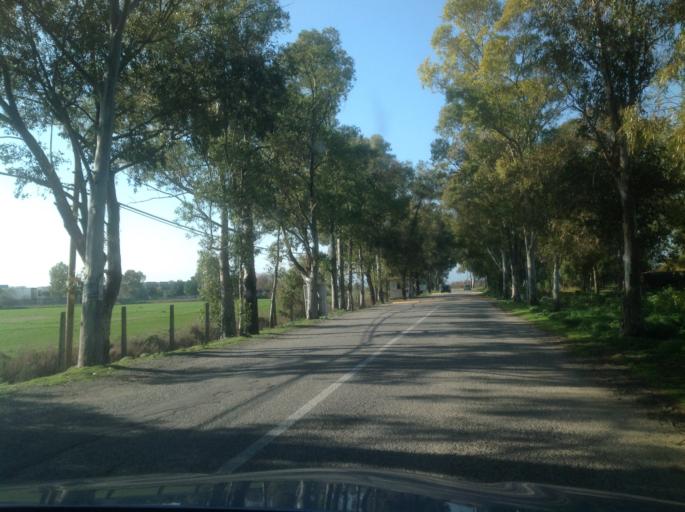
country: IT
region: Calabria
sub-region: Provincia di Cosenza
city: Sibari
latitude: 39.7261
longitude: 16.4988
